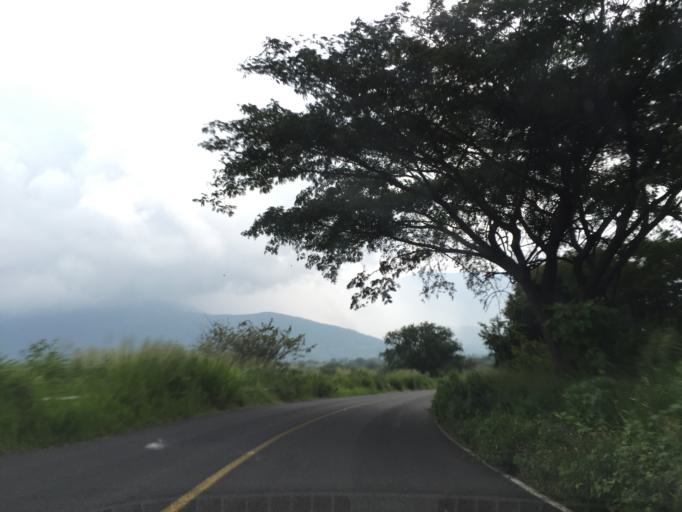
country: MX
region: Colima
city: Comala
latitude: 19.3424
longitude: -103.7824
